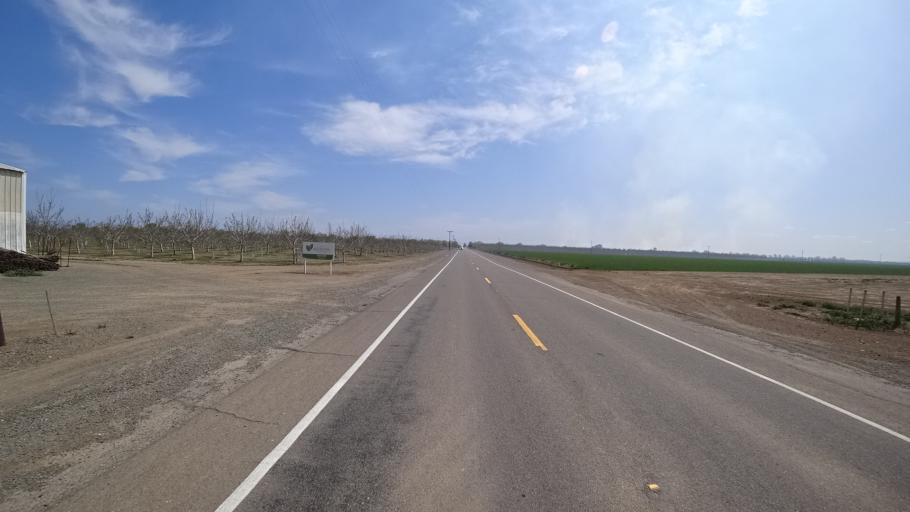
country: US
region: California
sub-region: Butte County
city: Durham
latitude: 39.4642
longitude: -121.9346
